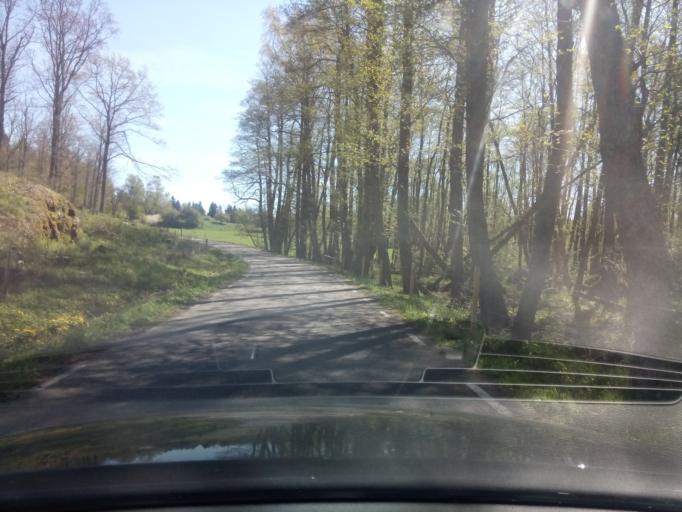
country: SE
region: Soedermanland
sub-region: Trosa Kommun
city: Trosa
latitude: 58.7975
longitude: 17.3735
